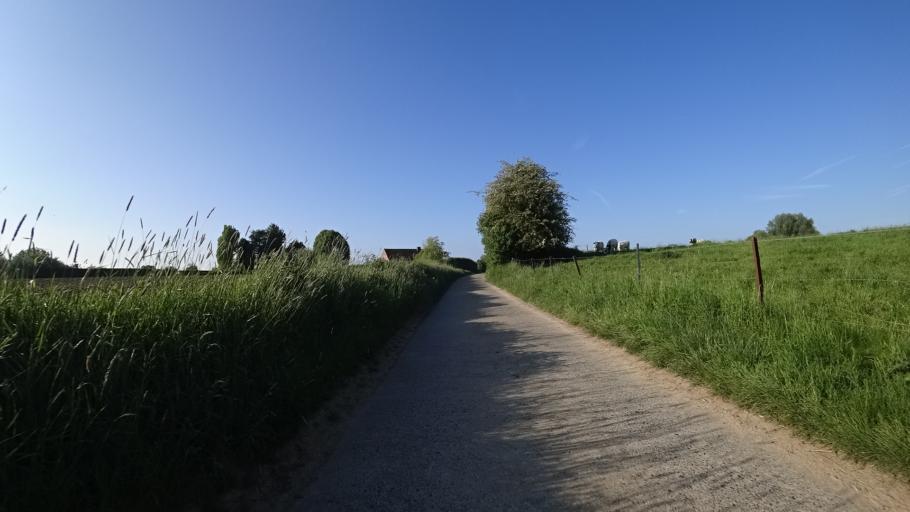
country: BE
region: Wallonia
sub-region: Province du Brabant Wallon
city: Walhain-Saint-Paul
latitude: 50.6165
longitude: 4.7154
